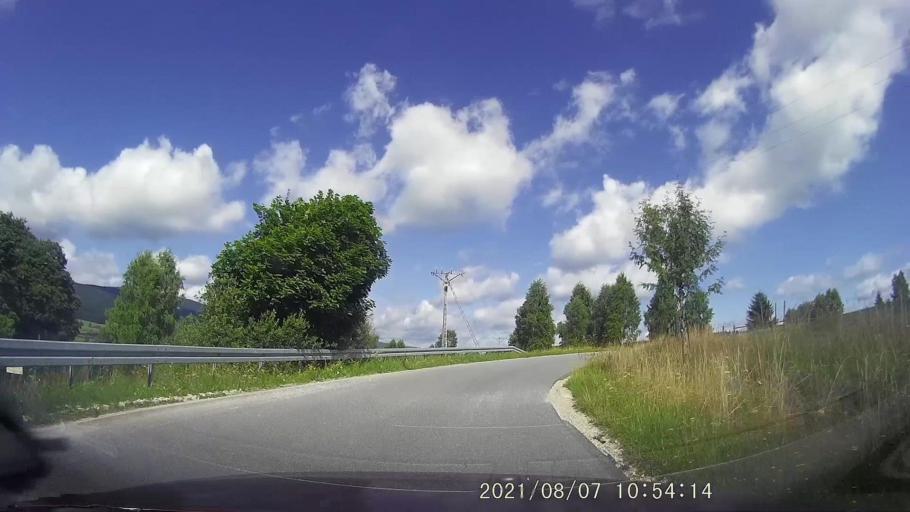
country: CZ
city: Rokytnice v Orlickych Horach
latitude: 50.2722
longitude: 16.4866
